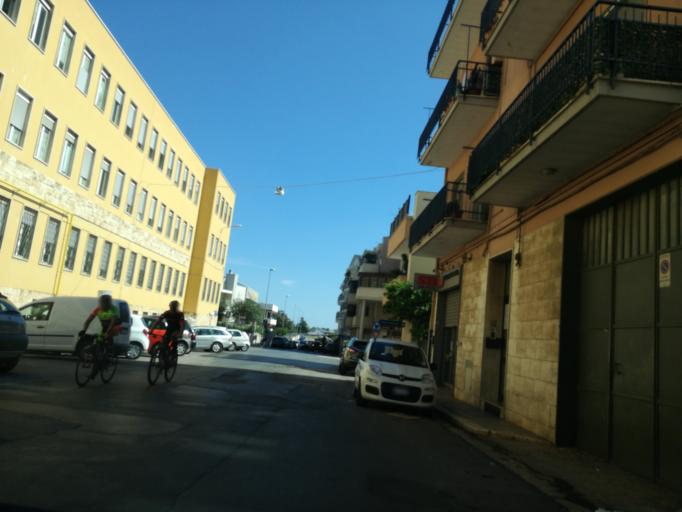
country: IT
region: Apulia
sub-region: Provincia di Bari
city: Castellana
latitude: 40.8882
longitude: 17.1677
